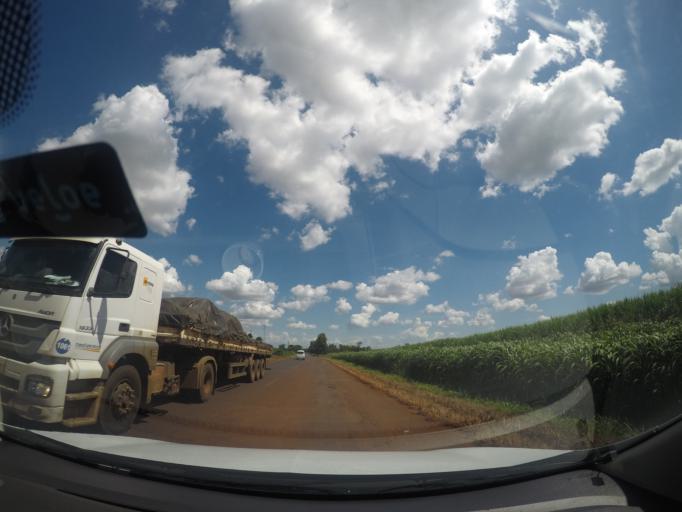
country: BR
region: Minas Gerais
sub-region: Frutal
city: Frutal
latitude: -19.8353
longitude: -48.7353
